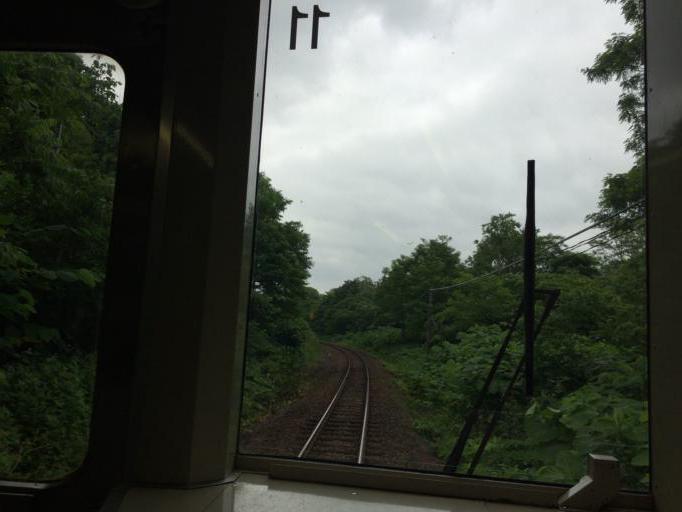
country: JP
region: Hokkaido
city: Yoichi
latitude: 43.1212
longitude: 140.7323
